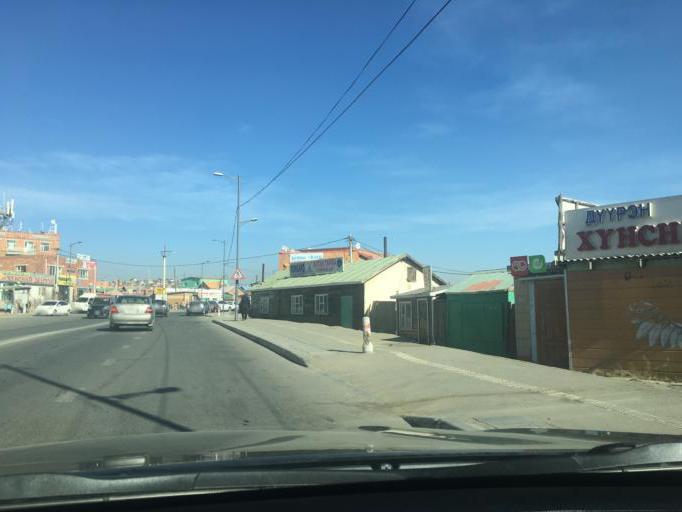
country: MN
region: Ulaanbaatar
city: Ulaanbaatar
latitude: 47.9178
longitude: 106.7811
